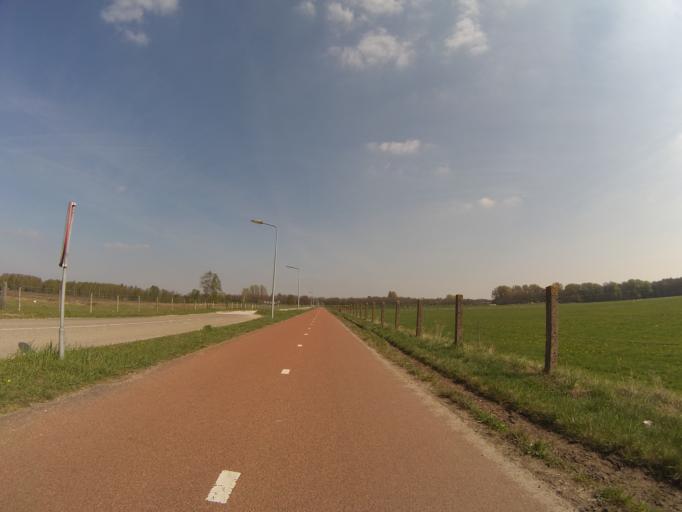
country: NL
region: North Holland
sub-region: Gemeente Blaricum
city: Blaricum
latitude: 52.2795
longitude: 5.2582
